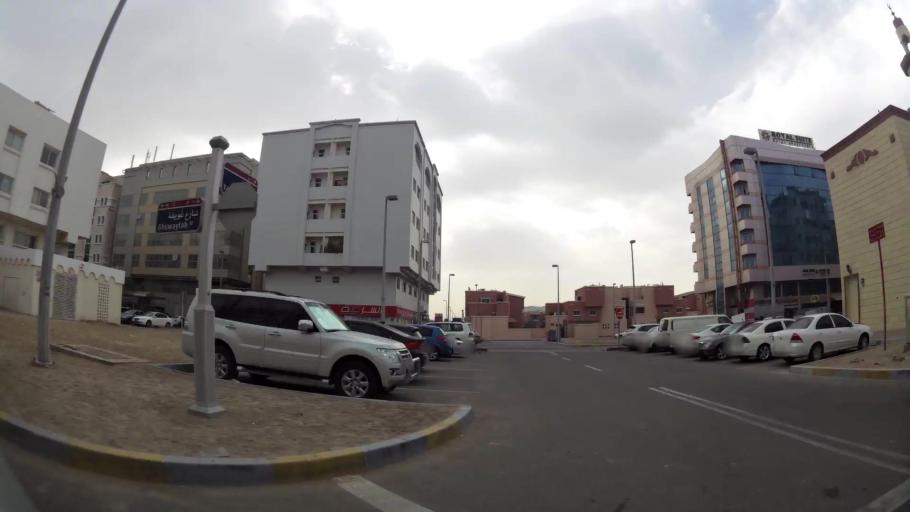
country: AE
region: Abu Dhabi
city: Abu Dhabi
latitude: 24.4752
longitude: 54.3791
